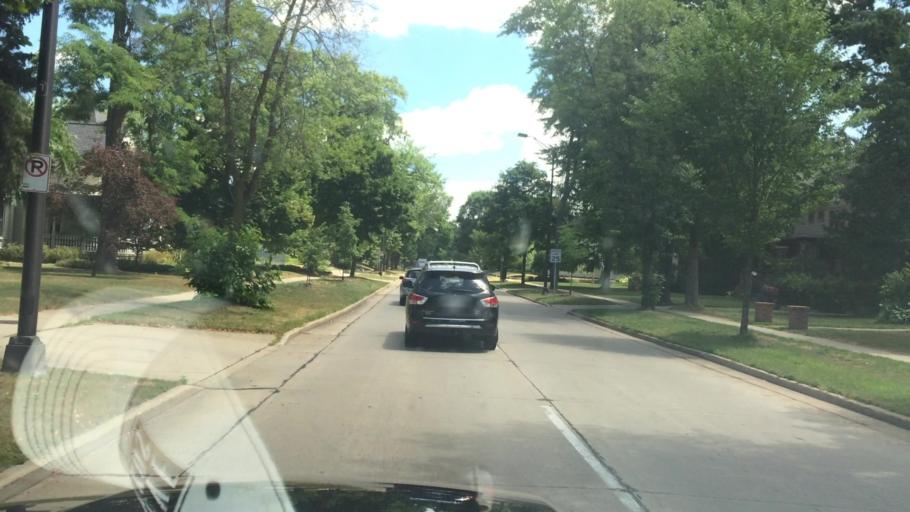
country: US
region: Wisconsin
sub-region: Portage County
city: Stevens Point
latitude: 44.5224
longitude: -89.5745
